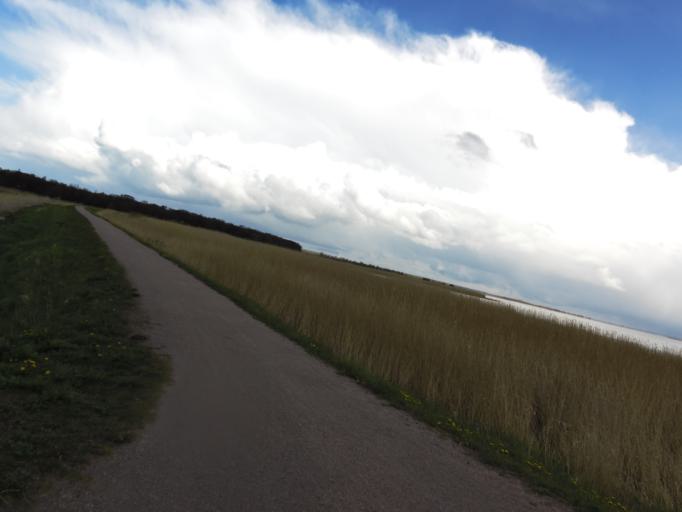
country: DE
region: Mecklenburg-Vorpommern
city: Saal
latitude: 54.3777
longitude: 12.4338
